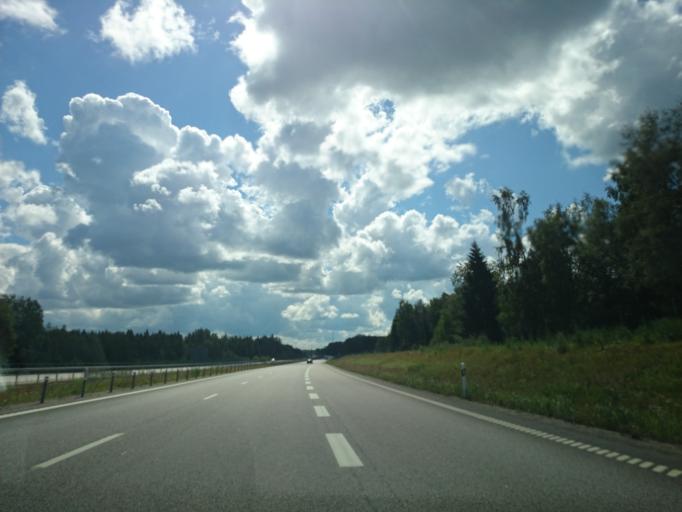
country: SE
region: Uppsala
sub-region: Alvkarleby Kommun
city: AElvkarleby
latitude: 60.4596
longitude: 17.4143
